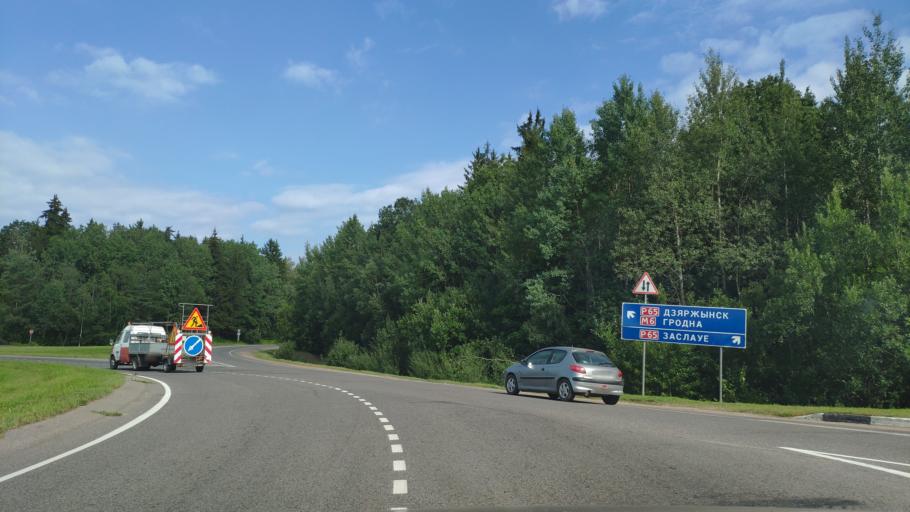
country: BY
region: Minsk
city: Khatsyezhyna
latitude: 53.9137
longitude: 27.2571
